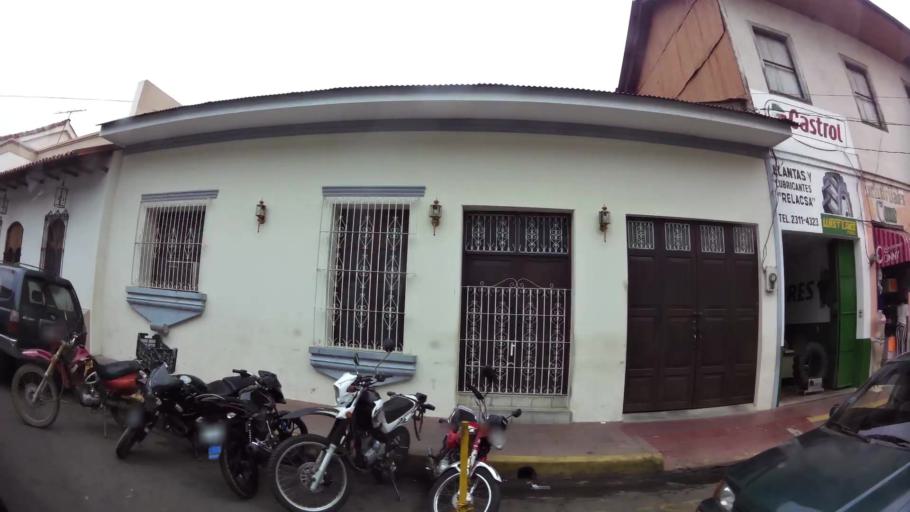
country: NI
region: Leon
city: Leon
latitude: 12.4362
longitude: -86.8755
